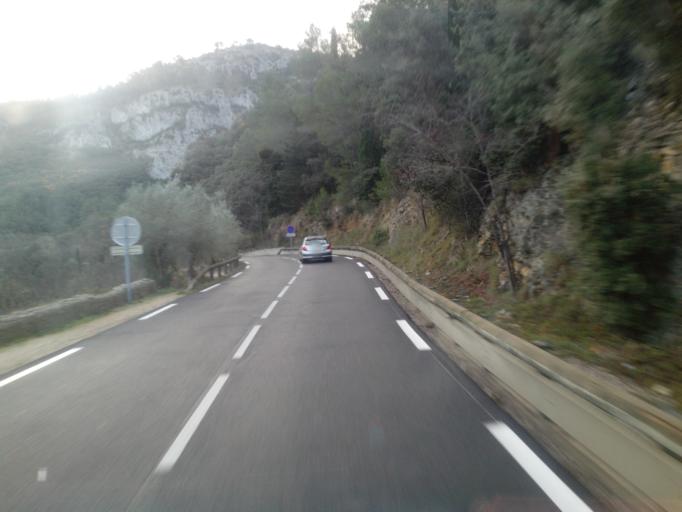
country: FR
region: Languedoc-Roussillon
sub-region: Departement de l'Herault
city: Saint-Jean-de-Fos
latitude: 43.7278
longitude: 3.5506
